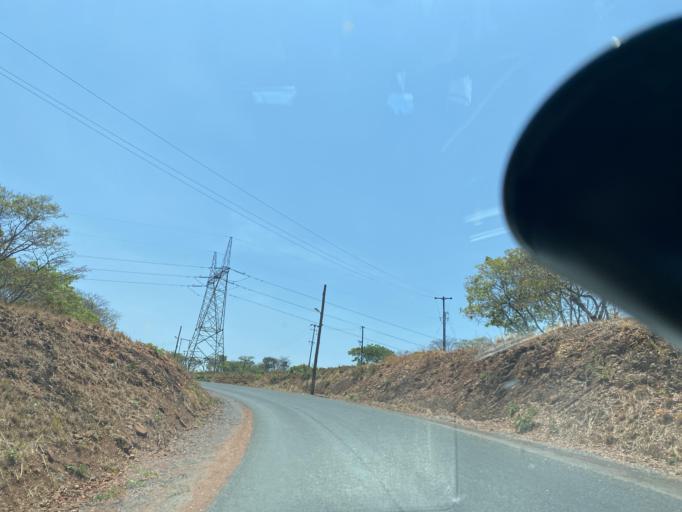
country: ZM
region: Lusaka
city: Kafue
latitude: -15.8659
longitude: 28.4516
